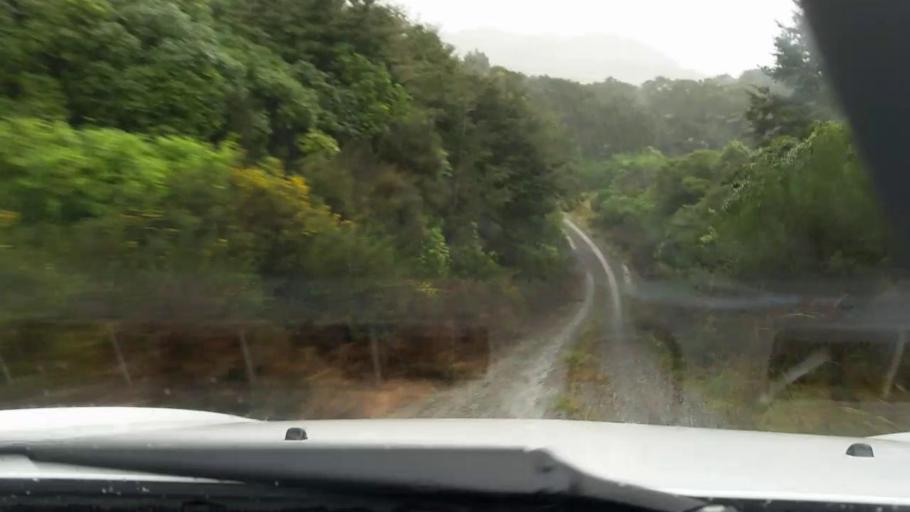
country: NZ
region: Wellington
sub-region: Masterton District
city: Masterton
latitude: -41.1594
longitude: 175.8009
